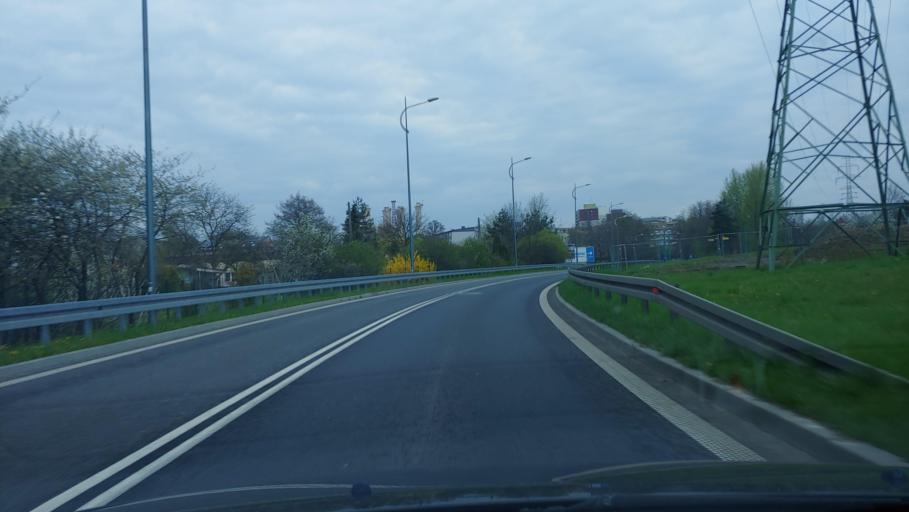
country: PL
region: Silesian Voivodeship
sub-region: Tychy
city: Cielmice
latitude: 50.0990
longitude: 19.0035
